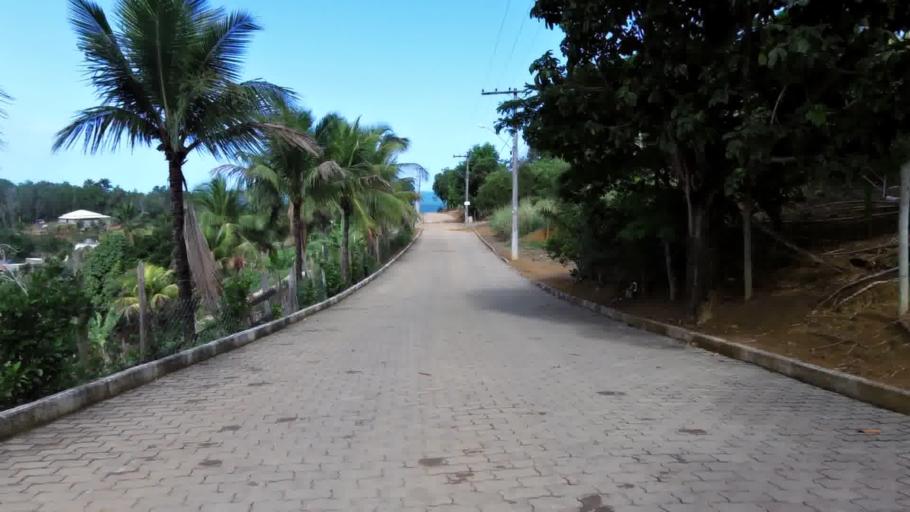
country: BR
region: Espirito Santo
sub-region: Piuma
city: Piuma
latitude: -20.8242
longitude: -40.6881
